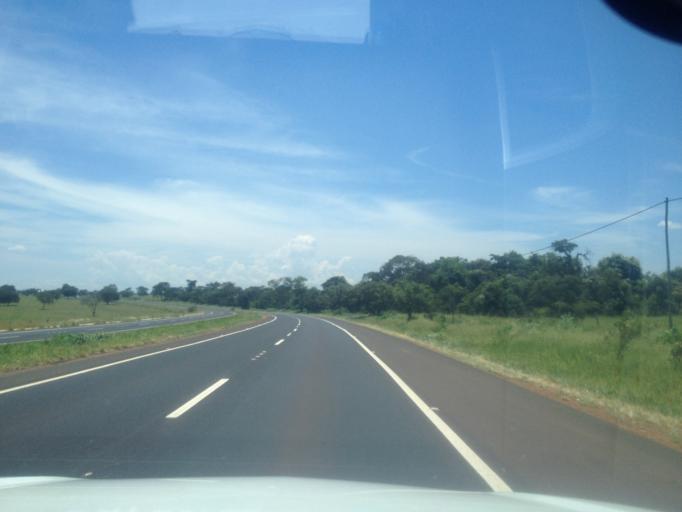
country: BR
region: Minas Gerais
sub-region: Monte Alegre De Minas
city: Monte Alegre de Minas
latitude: -18.8941
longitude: -48.6594
